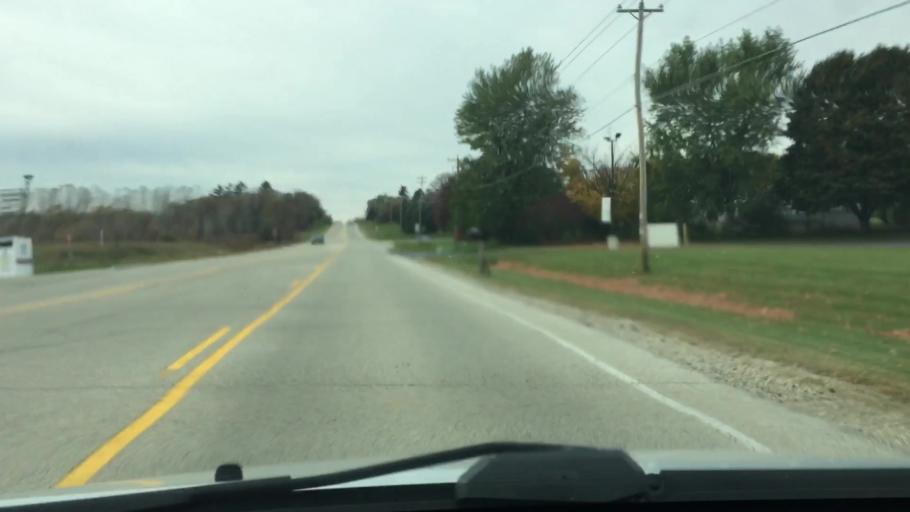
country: US
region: Wisconsin
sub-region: Waukesha County
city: Mukwonago
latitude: 42.8796
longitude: -88.2980
